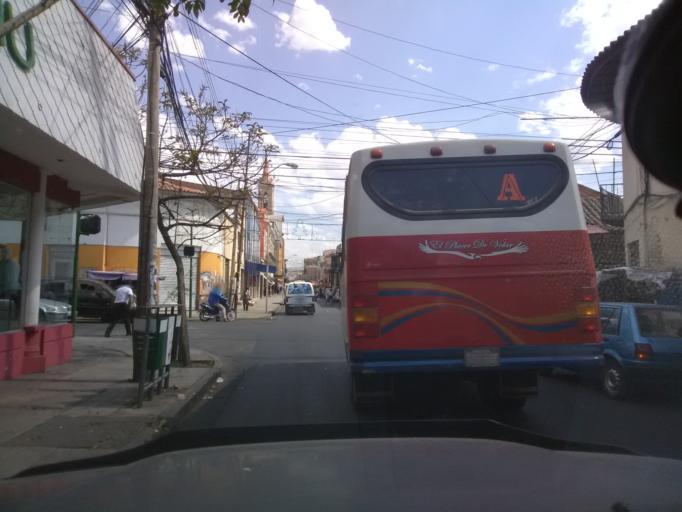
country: BO
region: Cochabamba
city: Cochabamba
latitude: -17.3896
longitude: -66.1560
